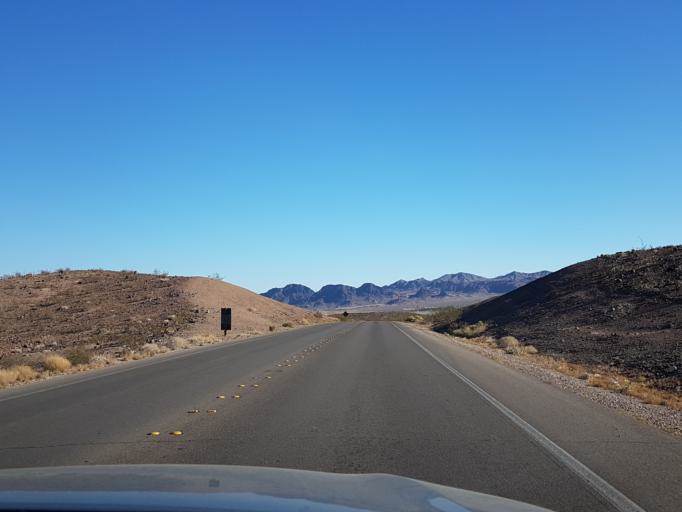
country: US
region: Nevada
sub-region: Clark County
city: Boulder City
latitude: 36.0763
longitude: -114.8219
